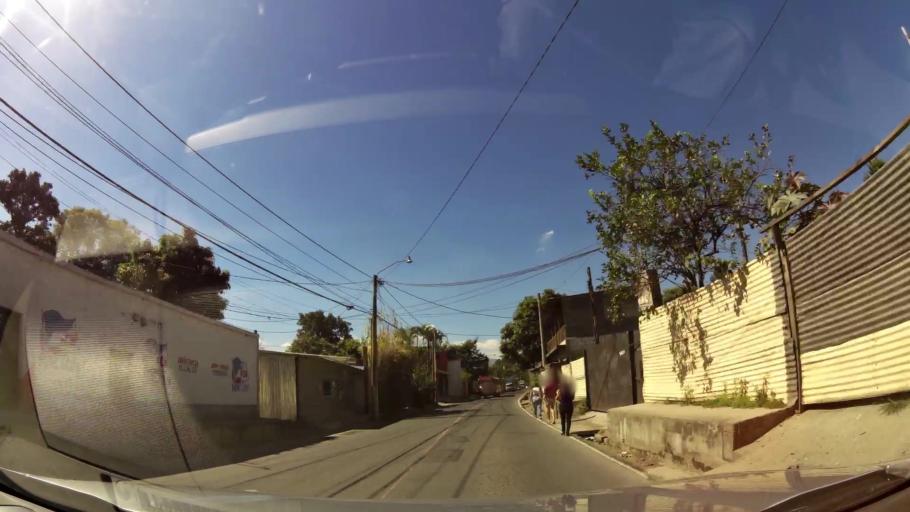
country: GT
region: Guatemala
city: Petapa
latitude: 14.4919
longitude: -90.5532
